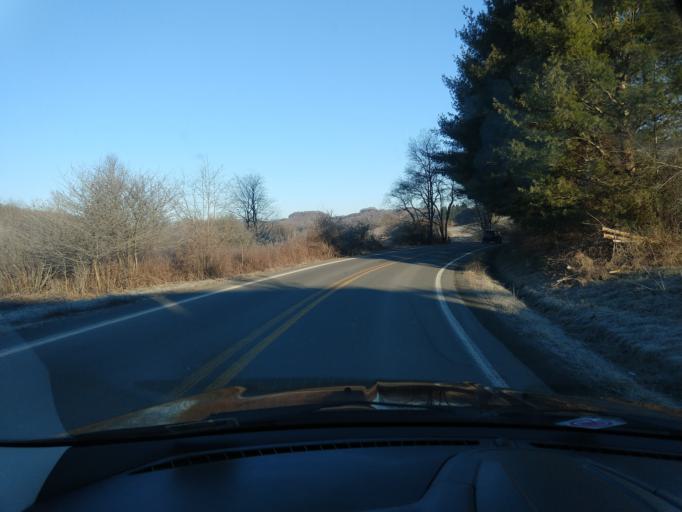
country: US
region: West Virginia
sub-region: Greenbrier County
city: Rainelle
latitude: 37.8581
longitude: -80.7182
